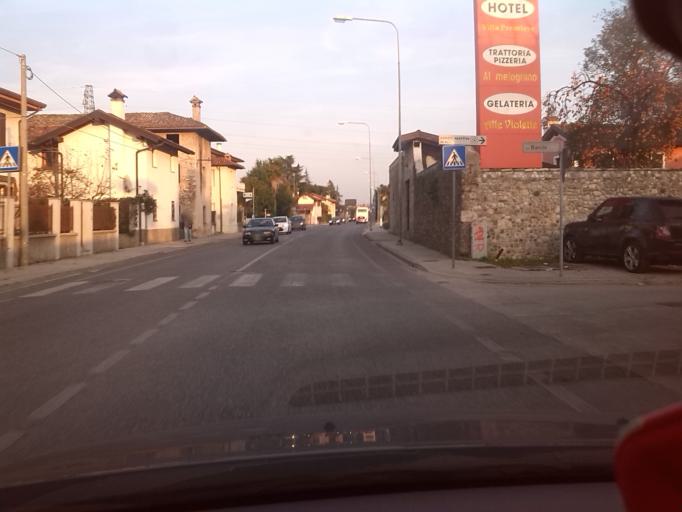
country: IT
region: Friuli Venezia Giulia
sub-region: Provincia di Udine
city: Udine
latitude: 46.0720
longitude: 13.2566
